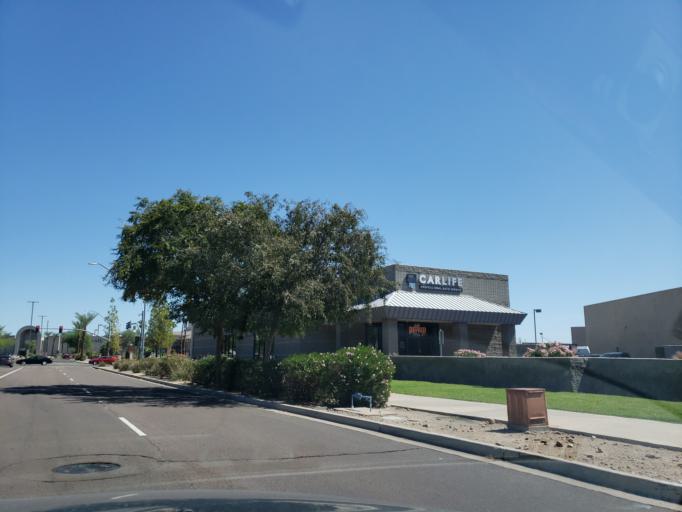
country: US
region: Arizona
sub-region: Maricopa County
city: Sun City
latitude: 33.6411
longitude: -112.2320
